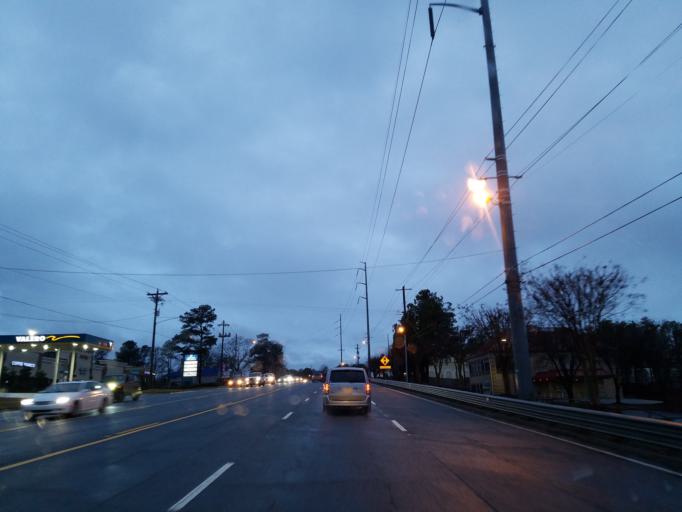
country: US
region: Georgia
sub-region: Fulton County
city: Roswell
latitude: 34.0188
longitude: -84.3138
